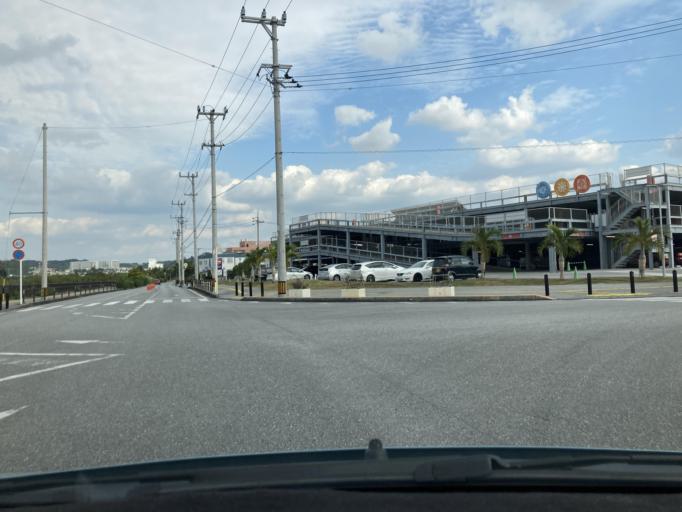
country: JP
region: Okinawa
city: Tomigusuku
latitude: 26.1602
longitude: 127.6577
